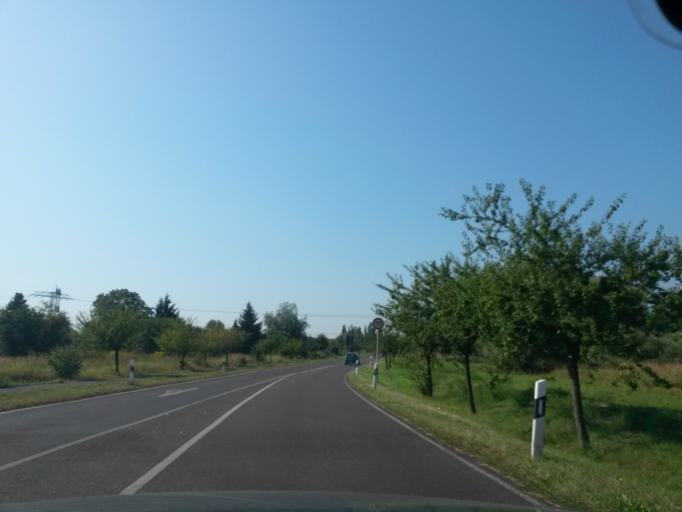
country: DE
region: Brandenburg
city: Angermunde
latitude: 53.0290
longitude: 13.9927
